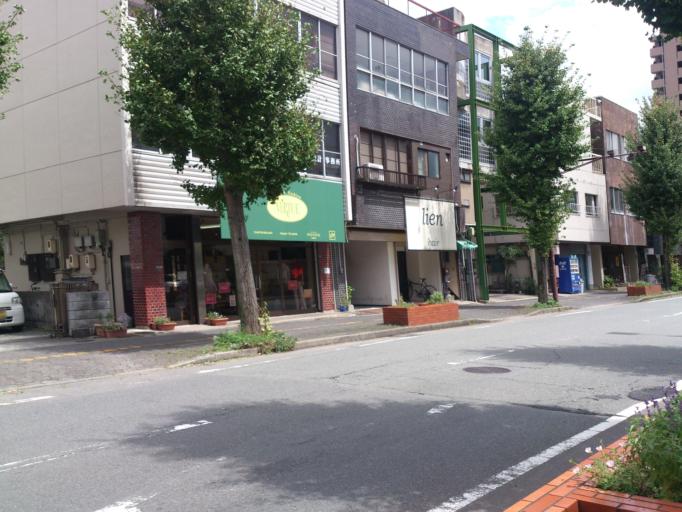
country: JP
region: Yamaguchi
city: Yamaguchi-shi
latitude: 34.1743
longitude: 131.4789
